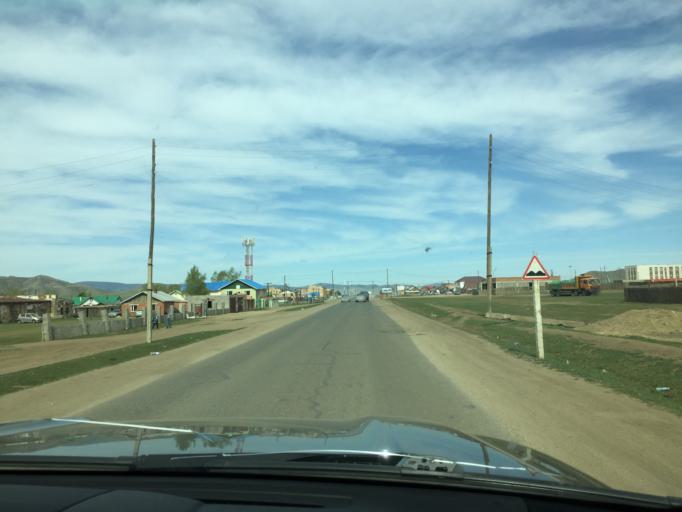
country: MN
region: Central Aimak
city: Ihsueuej
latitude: 48.2223
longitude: 106.2970
